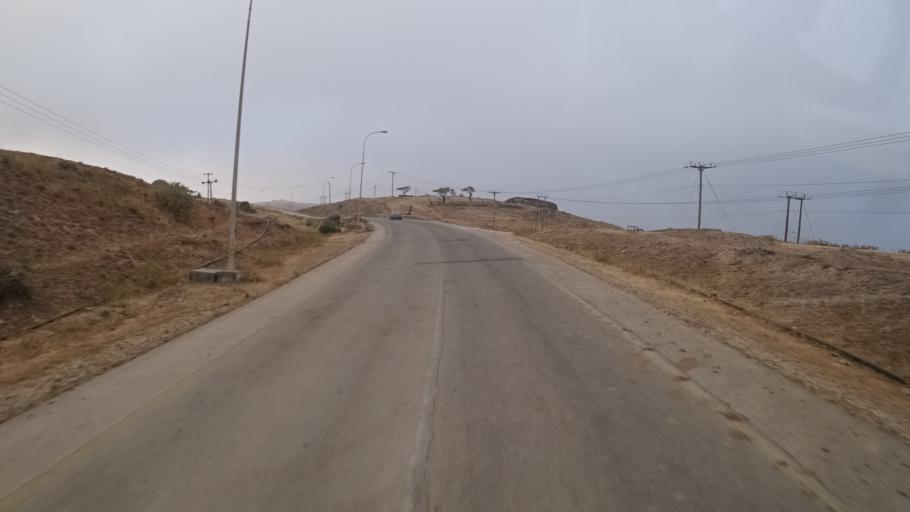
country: OM
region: Zufar
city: Salalah
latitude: 17.1298
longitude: 53.9769
